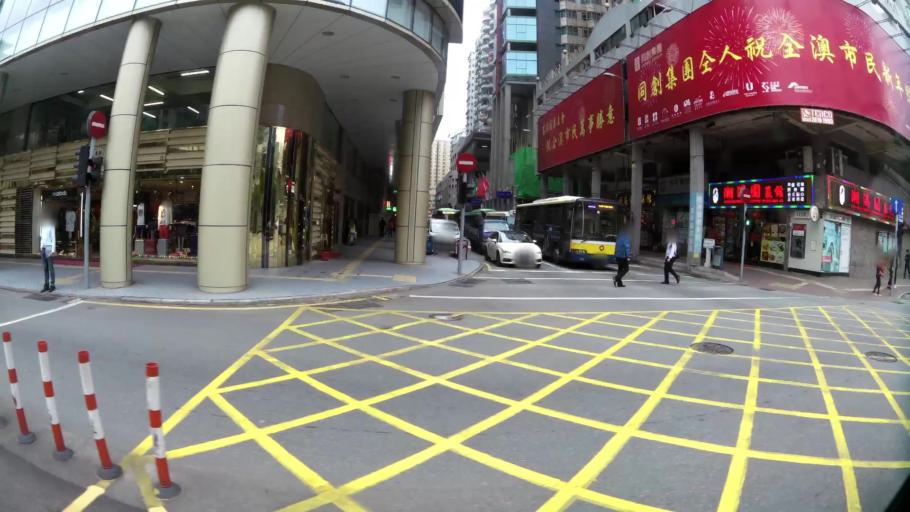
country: MO
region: Macau
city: Macau
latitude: 22.1926
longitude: 113.5489
